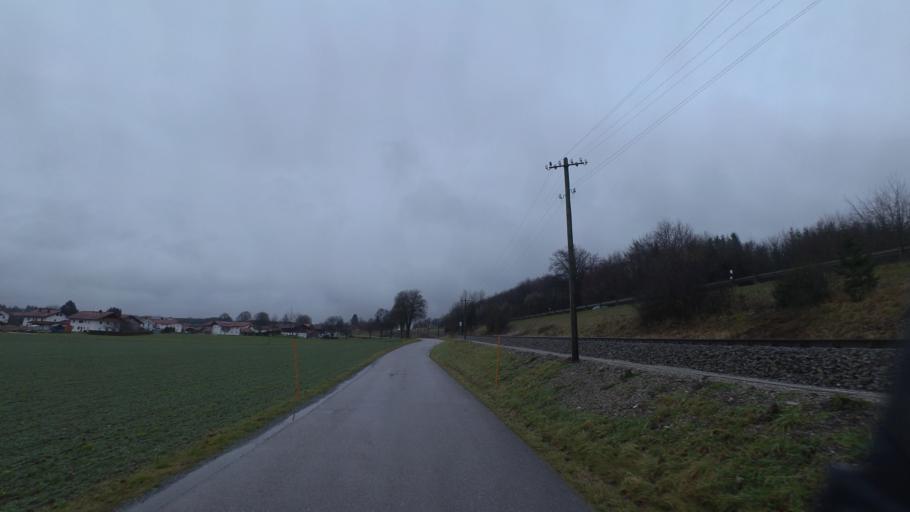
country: DE
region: Bavaria
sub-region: Upper Bavaria
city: Nussdorf
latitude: 47.9107
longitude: 12.6112
